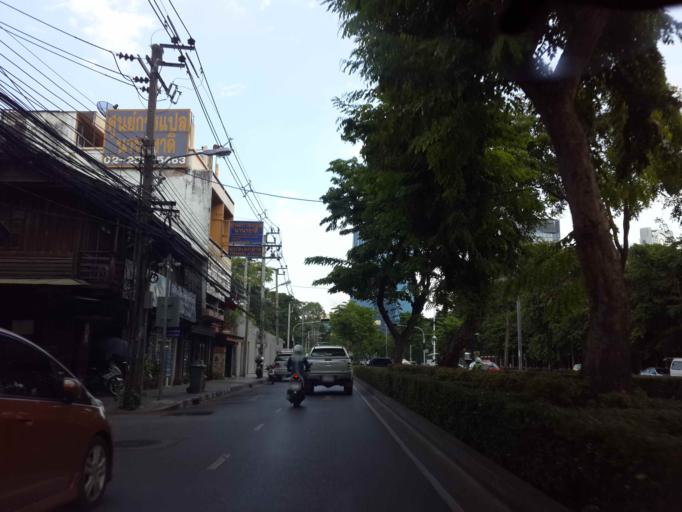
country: TH
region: Bangkok
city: Bang Rak
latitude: 13.7306
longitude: 100.5454
